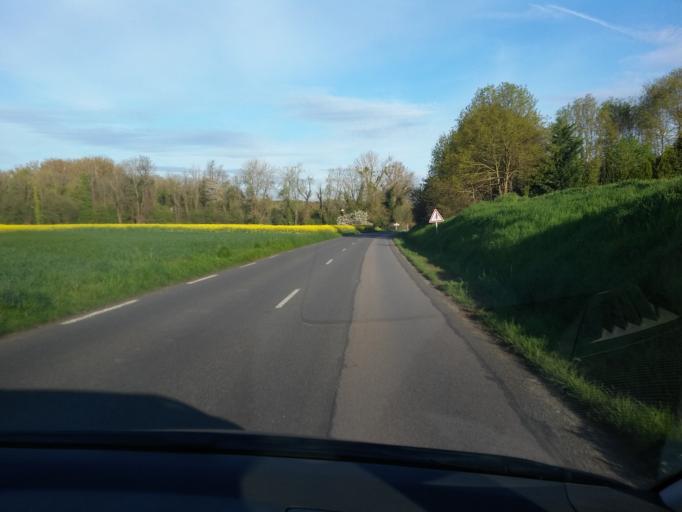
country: FR
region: Picardie
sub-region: Departement de l'Oise
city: Longueil-Sainte-Marie
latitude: 49.3488
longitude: 2.7255
